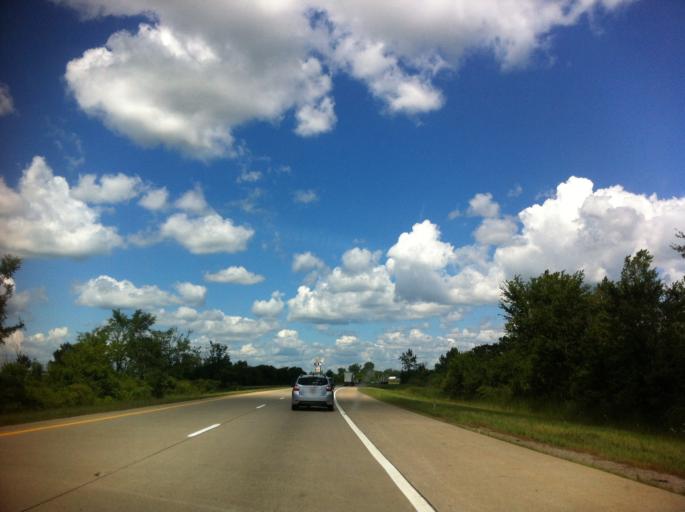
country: US
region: Michigan
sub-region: Monroe County
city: Lambertville
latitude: 41.7905
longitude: -83.6945
